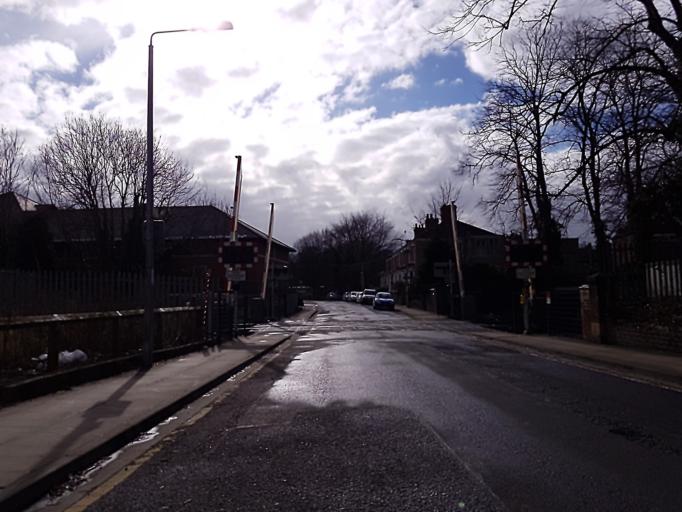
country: GB
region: England
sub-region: North East Lincolnshire
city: Grimbsy
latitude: 53.5637
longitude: -0.0915
